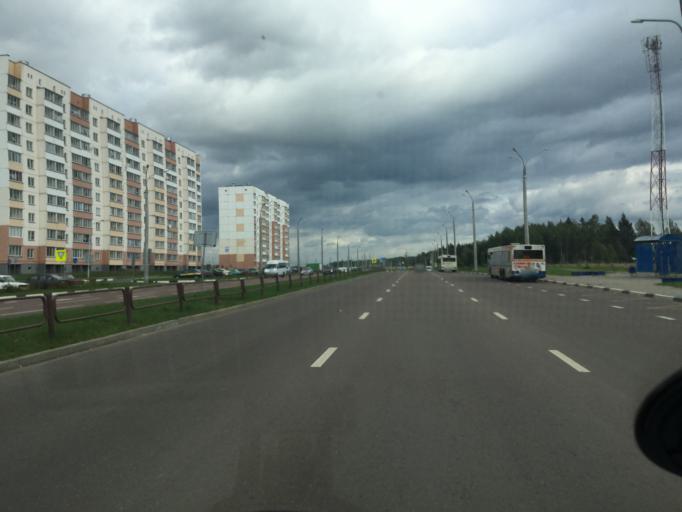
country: BY
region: Vitebsk
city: Vitebsk
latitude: 55.1652
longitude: 30.2867
